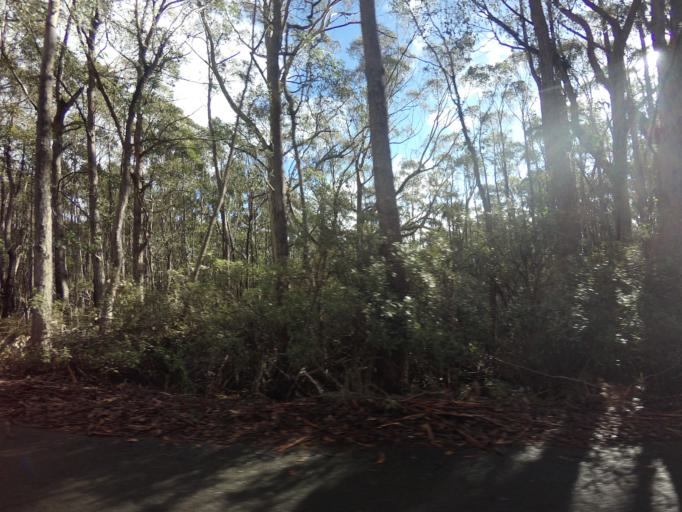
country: AU
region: Tasmania
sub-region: Glenorchy
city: Berriedale
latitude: -42.8415
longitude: 147.1493
